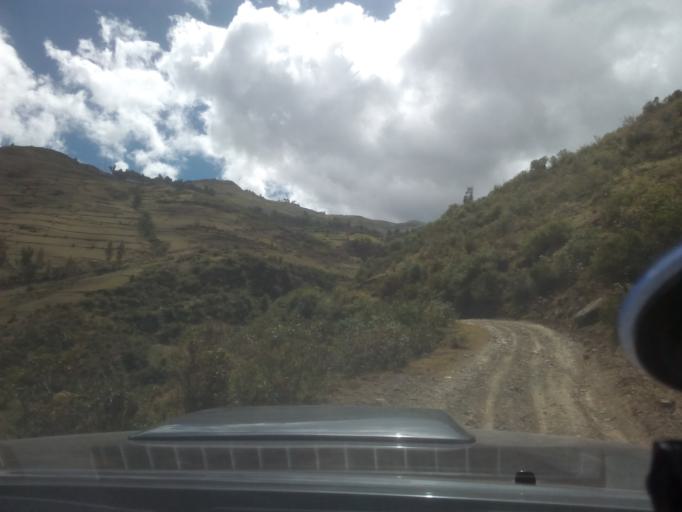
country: PE
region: Ayacucho
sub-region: Provincia de Huanta
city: Luricocha
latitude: -12.8829
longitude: -74.2195
